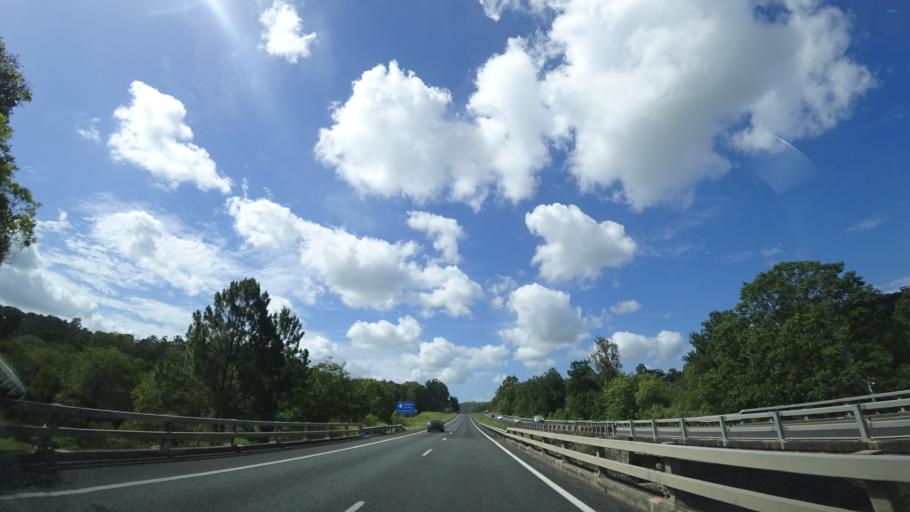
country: AU
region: Queensland
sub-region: Sunshine Coast
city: Twin Waters
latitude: -26.6309
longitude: 152.9879
